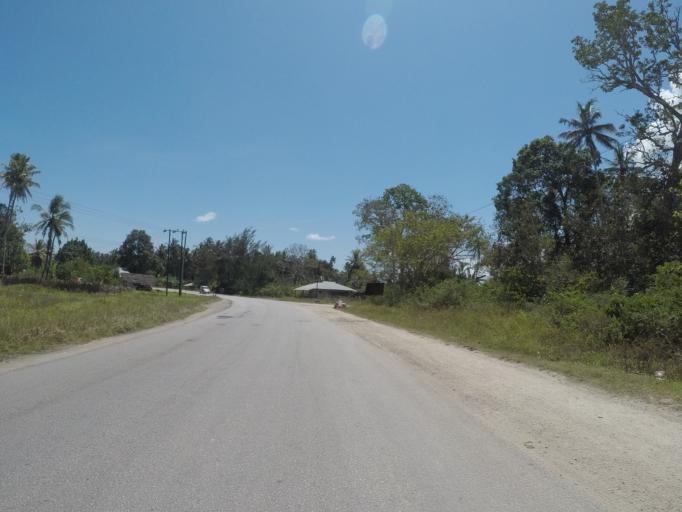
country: TZ
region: Zanzibar Central/South
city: Nganane
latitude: -6.2700
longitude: 39.4274
